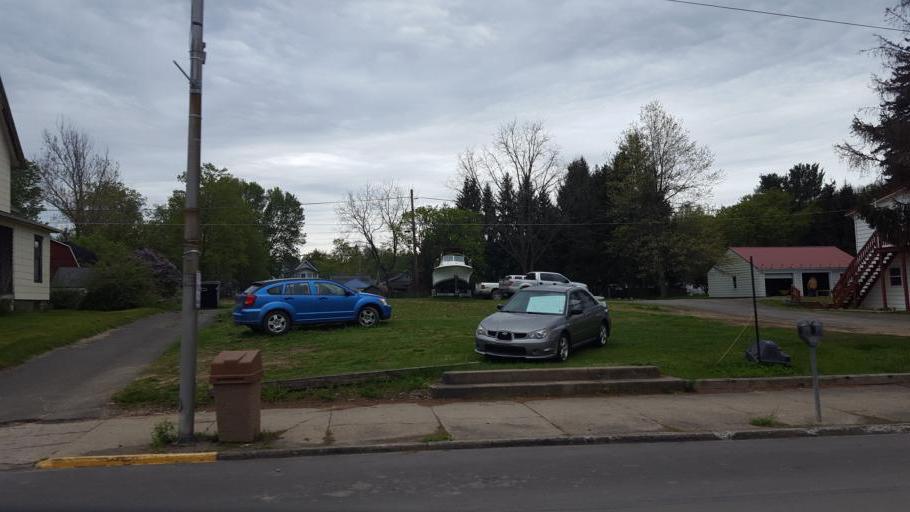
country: US
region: Pennsylvania
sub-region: Tioga County
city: Westfield
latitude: 41.9191
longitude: -77.5403
